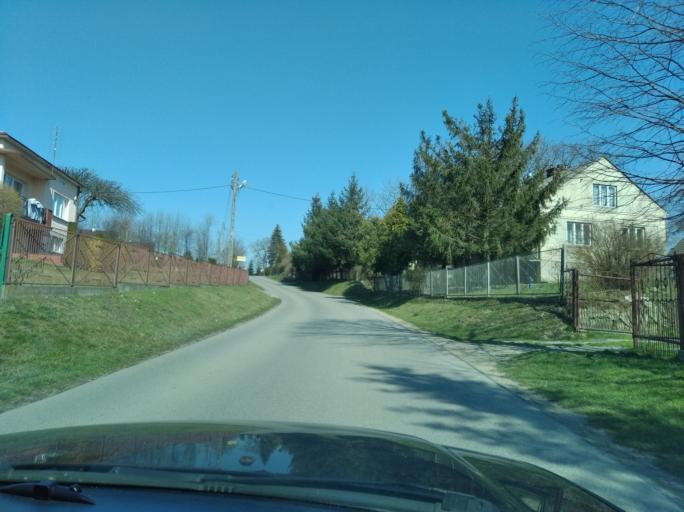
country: PL
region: Subcarpathian Voivodeship
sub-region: Powiat jaroslawski
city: Pawlosiow
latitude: 49.9626
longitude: 22.6468
